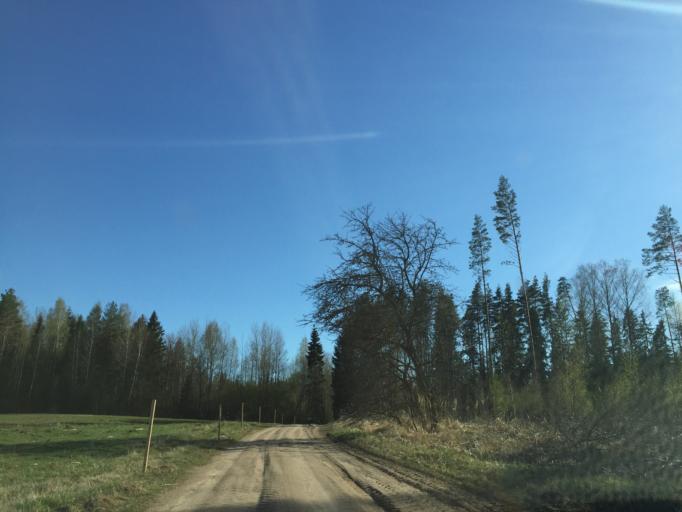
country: EE
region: Valgamaa
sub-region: Valga linn
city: Valga
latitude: 57.7777
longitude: 26.2318
